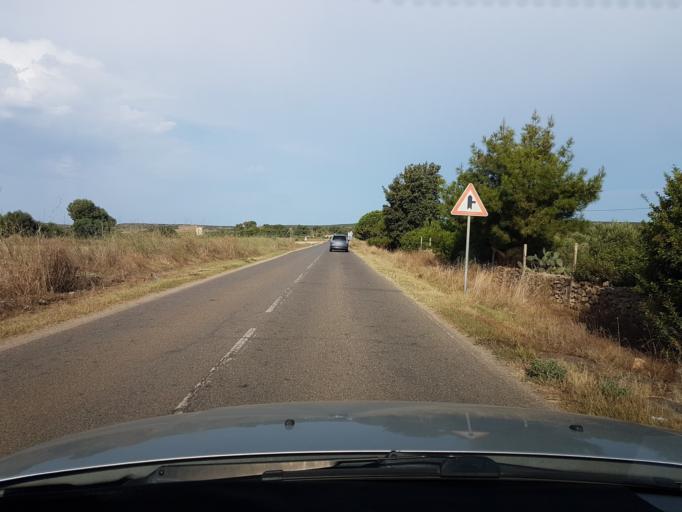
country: IT
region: Sardinia
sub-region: Provincia di Oristano
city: Cabras
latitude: 39.9158
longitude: 8.4547
